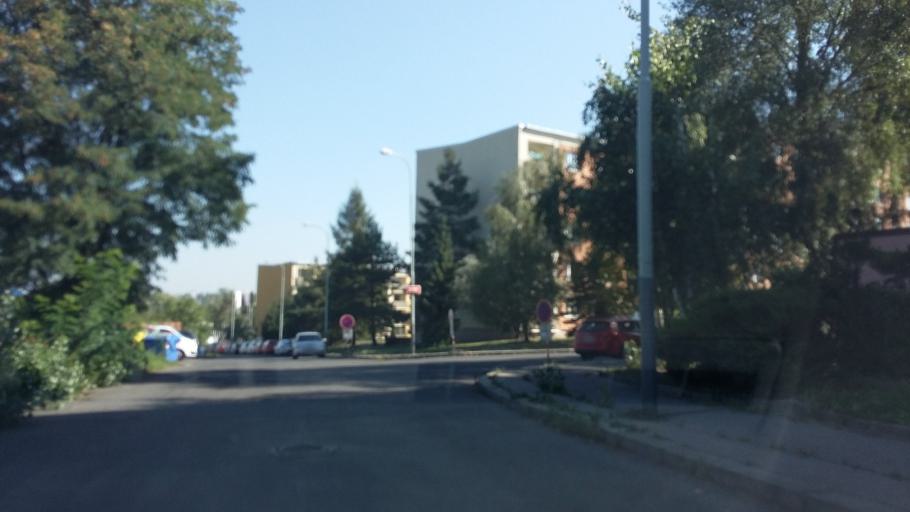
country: CZ
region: Praha
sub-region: Praha 9
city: Vysocany
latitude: 50.0577
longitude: 14.5176
